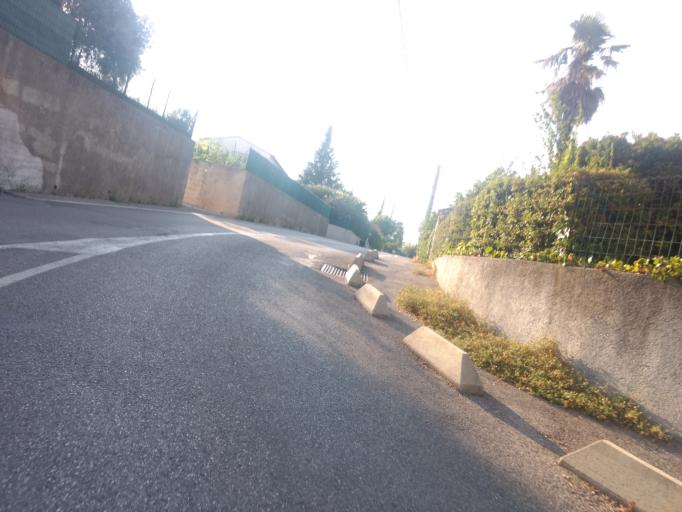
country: FR
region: Provence-Alpes-Cote d'Azur
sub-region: Departement des Alpes-de-Haute-Provence
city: Manosque
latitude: 43.8233
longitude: 5.7802
